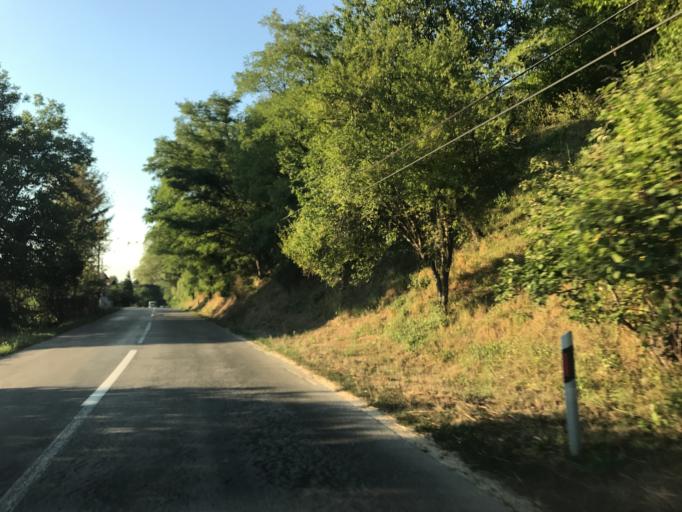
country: RO
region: Mehedinti
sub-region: Comuna Svinita
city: Svinita
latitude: 44.3750
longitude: 22.1785
